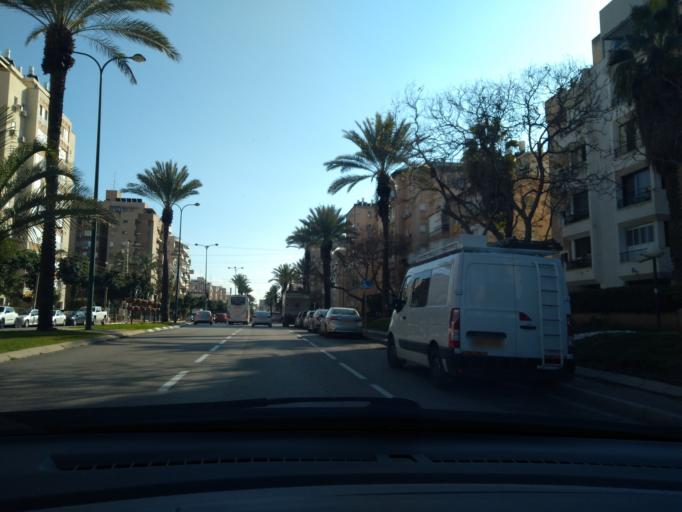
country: IL
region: Central District
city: Netanya
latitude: 32.3361
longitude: 34.8594
